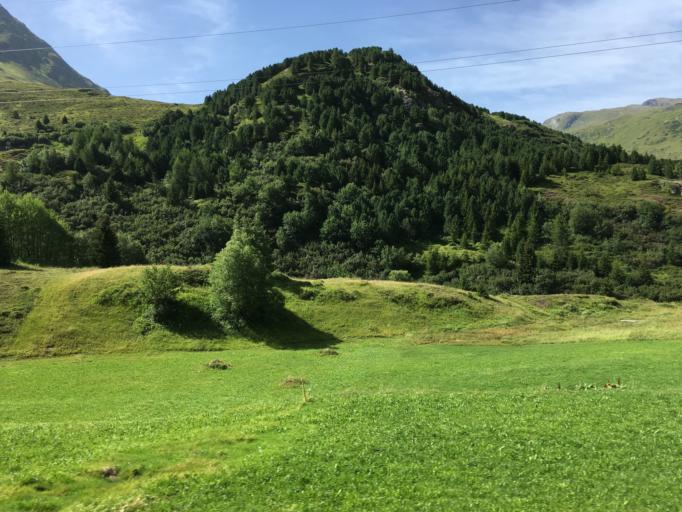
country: CH
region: Grisons
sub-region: Maloja District
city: Silvaplana
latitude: 46.4626
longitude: 9.6641
